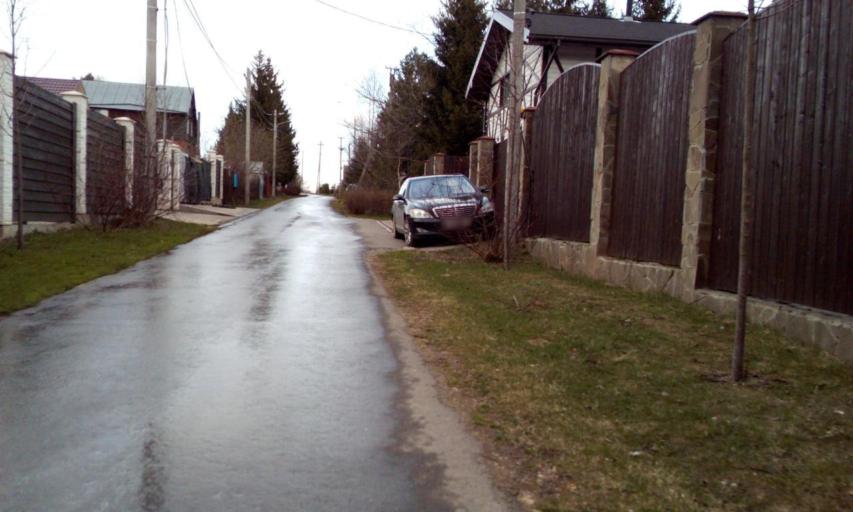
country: RU
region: Moskovskaya
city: Troitsk
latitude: 55.5197
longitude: 37.2634
